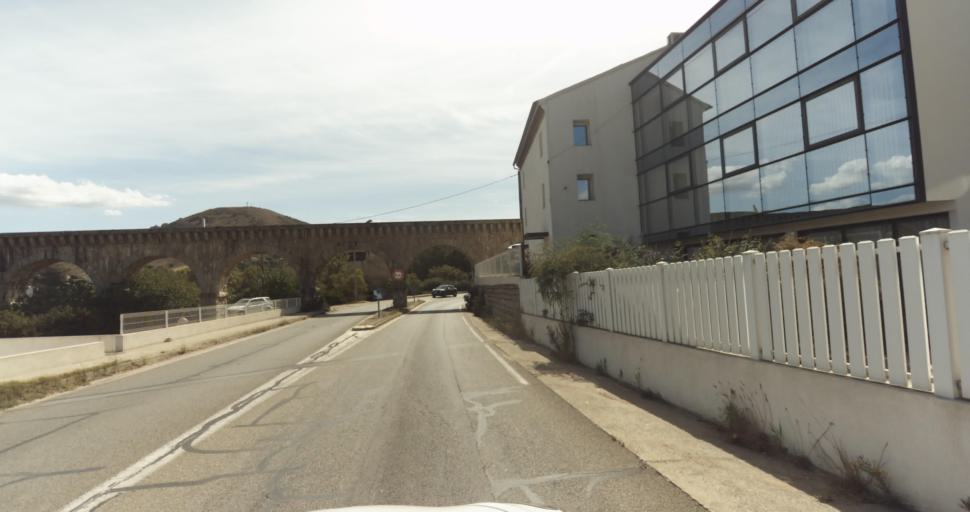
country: FR
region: Corsica
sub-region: Departement de la Corse-du-Sud
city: Afa
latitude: 41.9540
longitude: 8.7840
